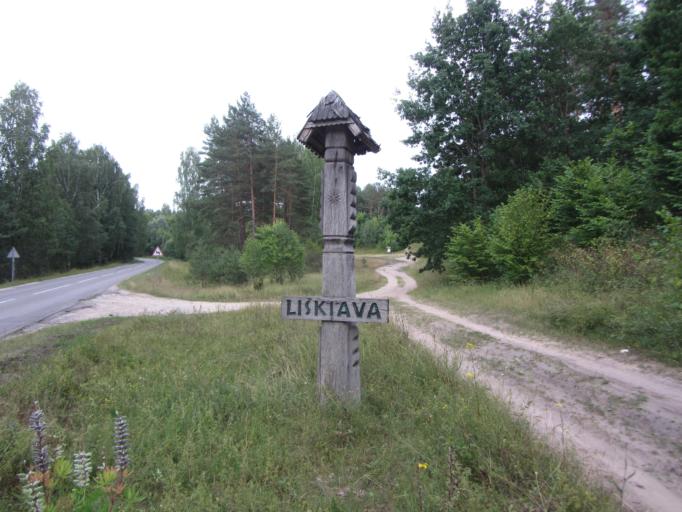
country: LT
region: Alytaus apskritis
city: Druskininkai
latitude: 54.0822
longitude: 24.0440
